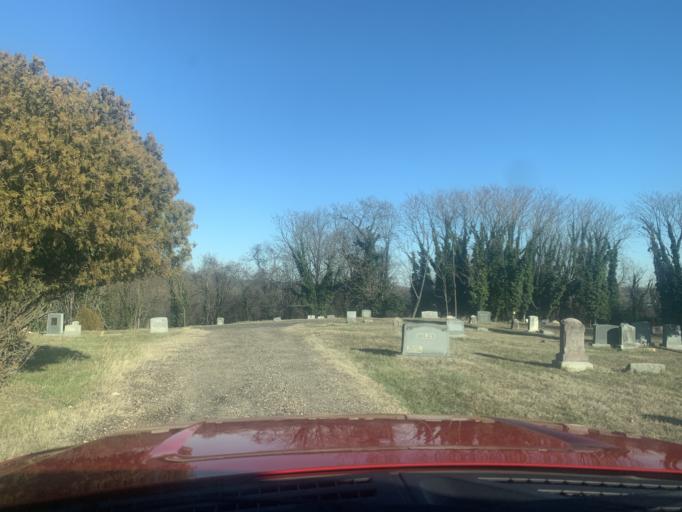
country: US
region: Maryland
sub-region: Anne Arundel County
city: Brooklyn Park
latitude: 39.2118
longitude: -76.6039
